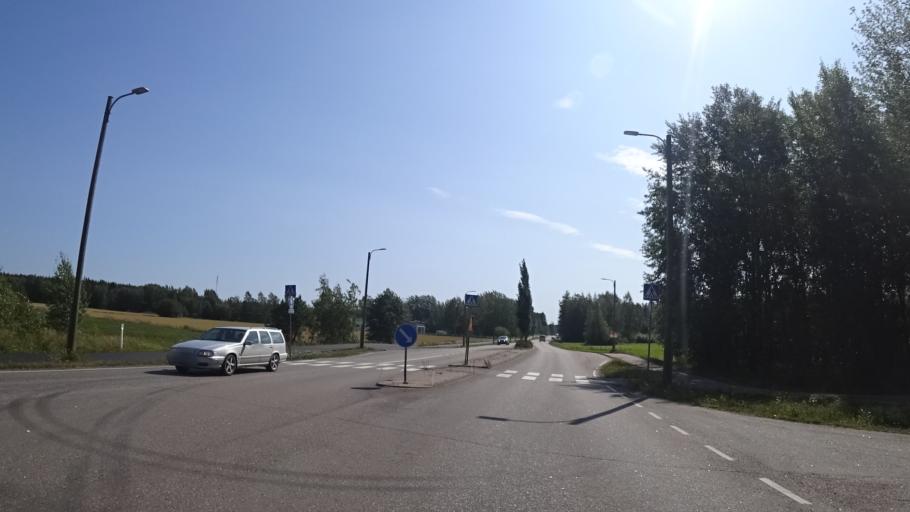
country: FI
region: Kymenlaakso
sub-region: Kotka-Hamina
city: Karhula
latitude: 60.5199
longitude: 26.9525
